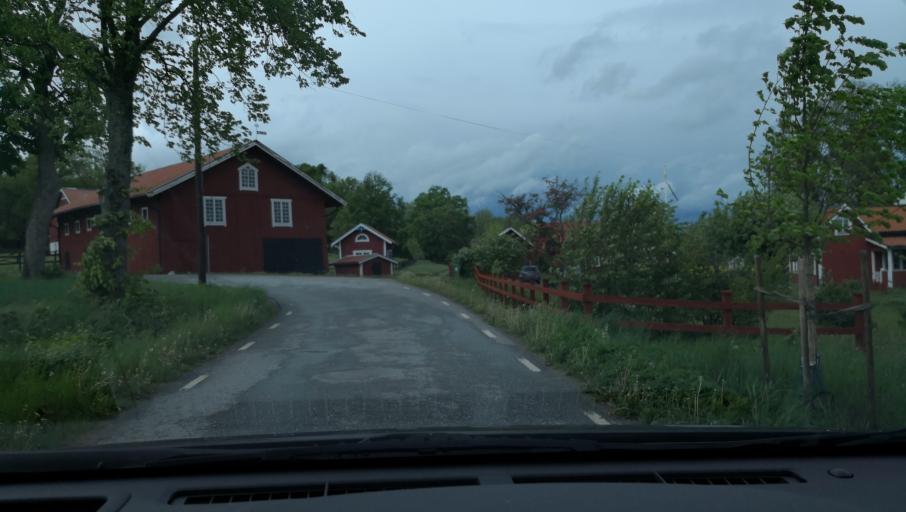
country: SE
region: Uppsala
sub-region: Enkopings Kommun
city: Orsundsbro
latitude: 59.7244
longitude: 17.4180
